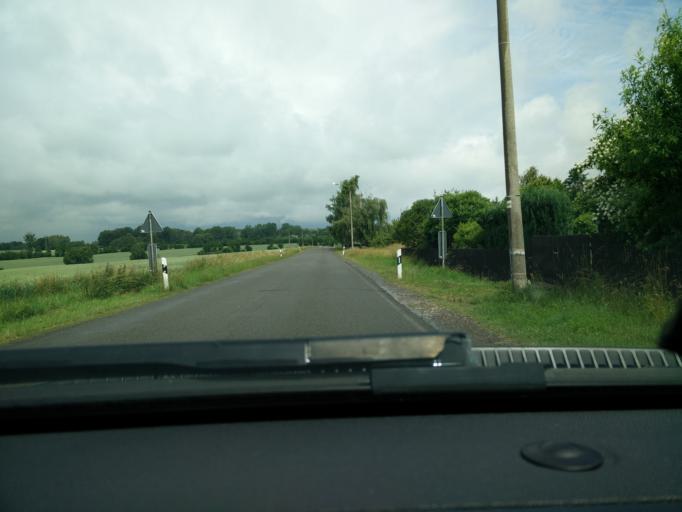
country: DE
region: Saxony
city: Geithain
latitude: 51.0625
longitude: 12.6906
